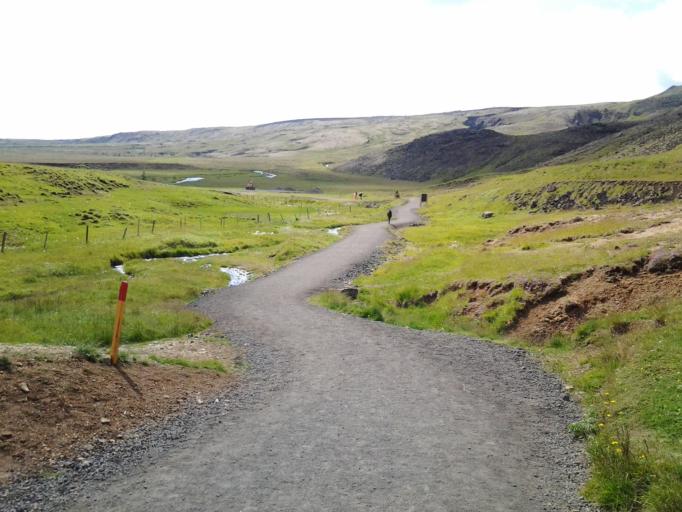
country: IS
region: South
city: Hveragerdi
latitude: 64.0254
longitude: -21.2120
